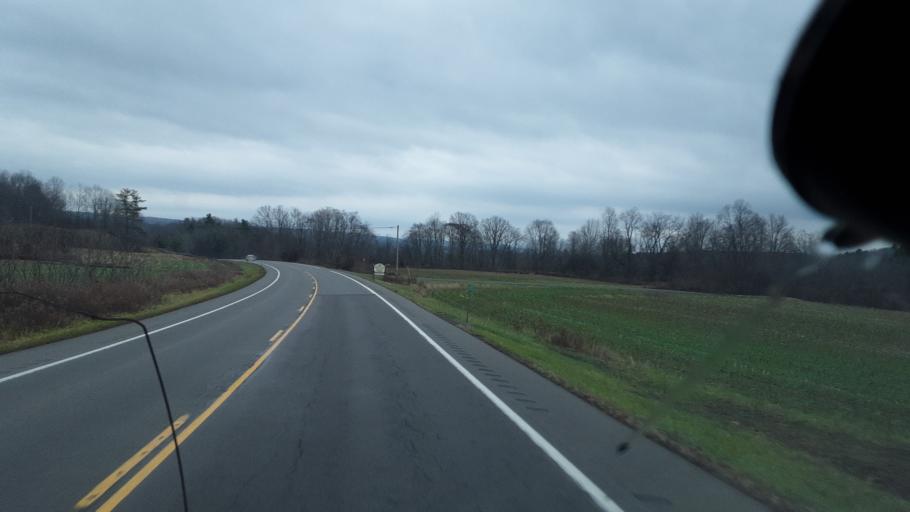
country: US
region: New York
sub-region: Allegany County
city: Houghton
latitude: 42.3905
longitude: -78.1660
